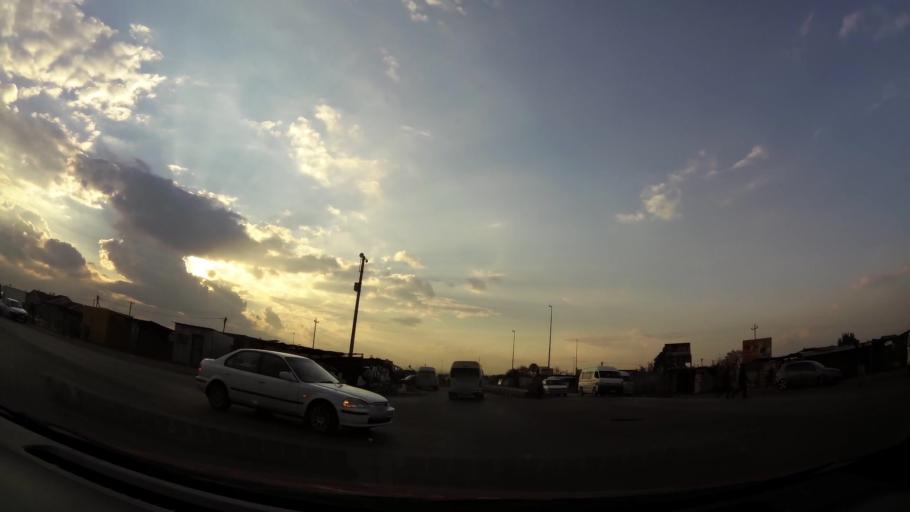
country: ZA
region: Gauteng
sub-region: City of Johannesburg Metropolitan Municipality
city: Orange Farm
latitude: -26.5635
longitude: 27.8337
